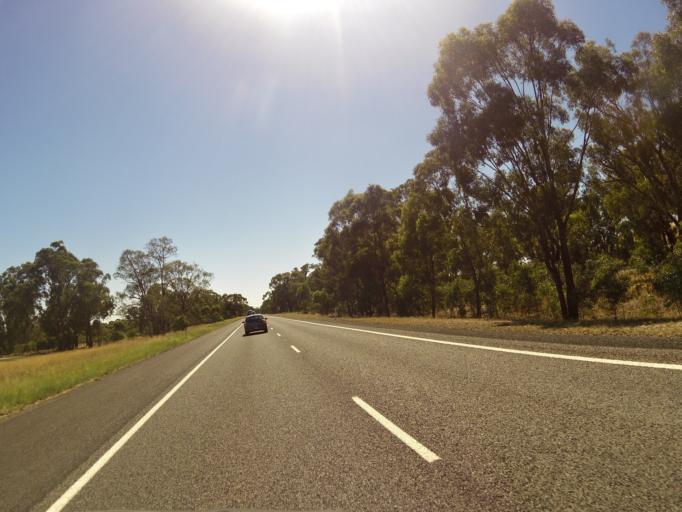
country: AU
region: Victoria
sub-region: Greater Shepparton
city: Shepparton
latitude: -36.8674
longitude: 145.2932
